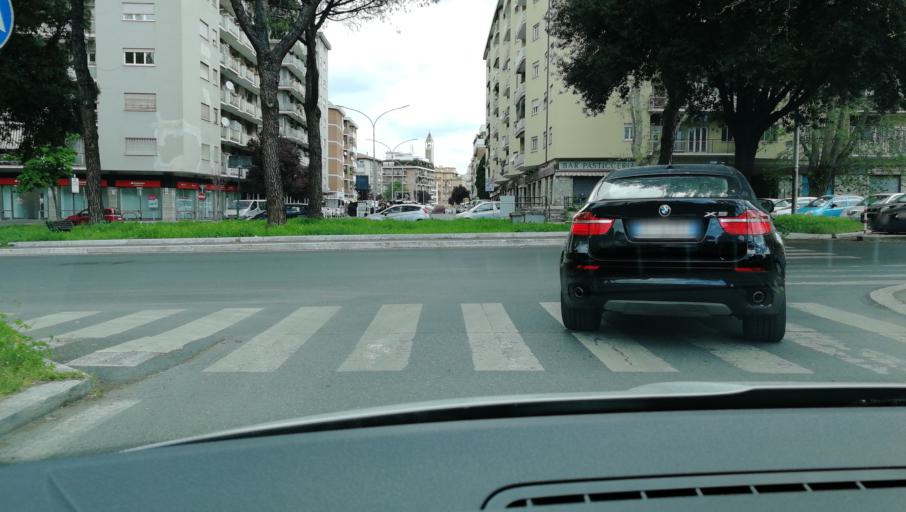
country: IT
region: Latium
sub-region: Citta metropolitana di Roma Capitale
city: Rome
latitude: 41.8509
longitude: 12.4928
